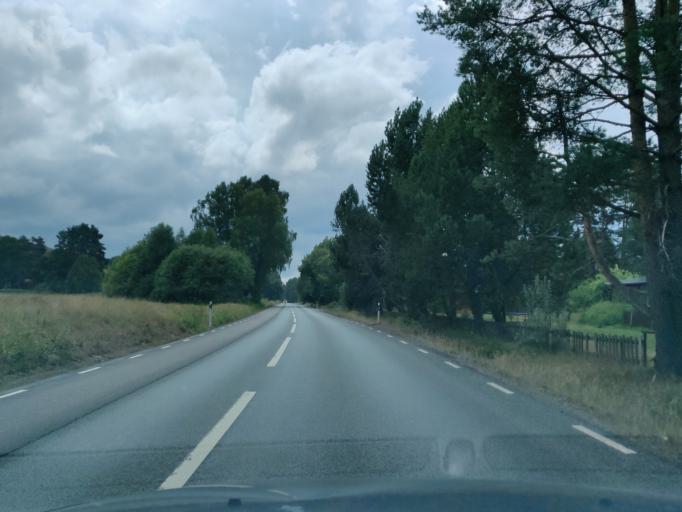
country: SE
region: Vaermland
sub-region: Munkfors Kommun
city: Munkfors
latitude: 59.9013
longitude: 13.5588
